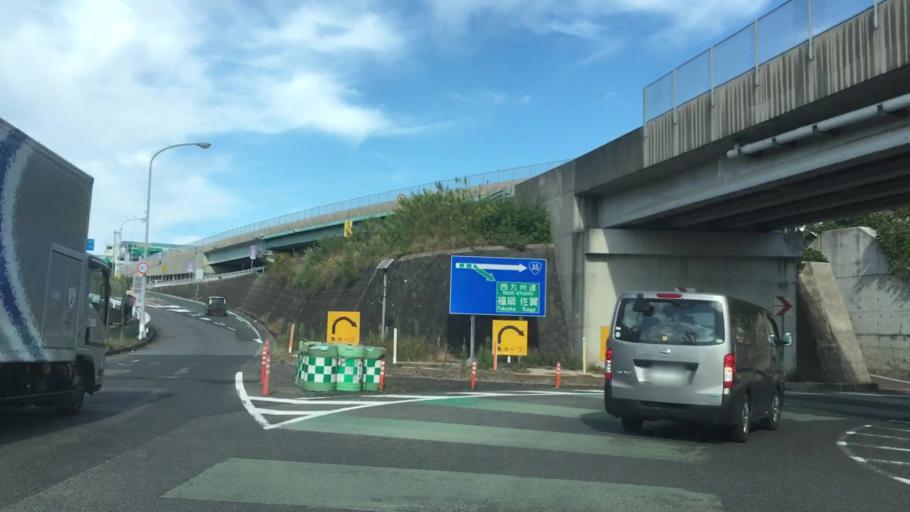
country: JP
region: Nagasaki
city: Sasebo
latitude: 33.1461
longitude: 129.7776
